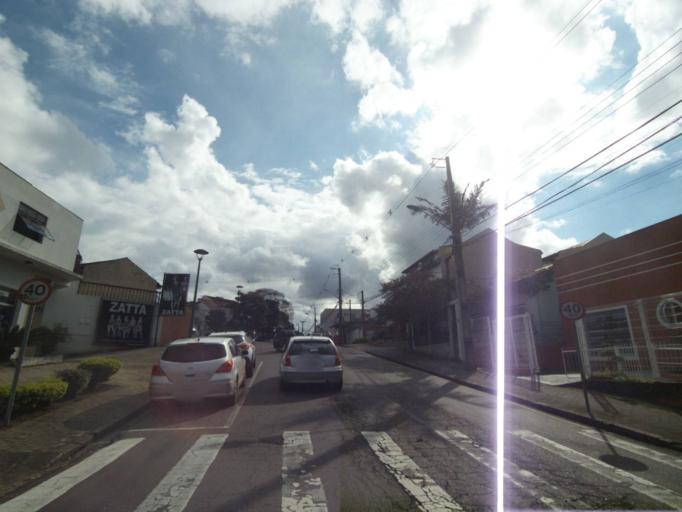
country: BR
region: Parana
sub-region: Curitiba
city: Curitiba
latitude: -25.4152
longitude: -49.2763
